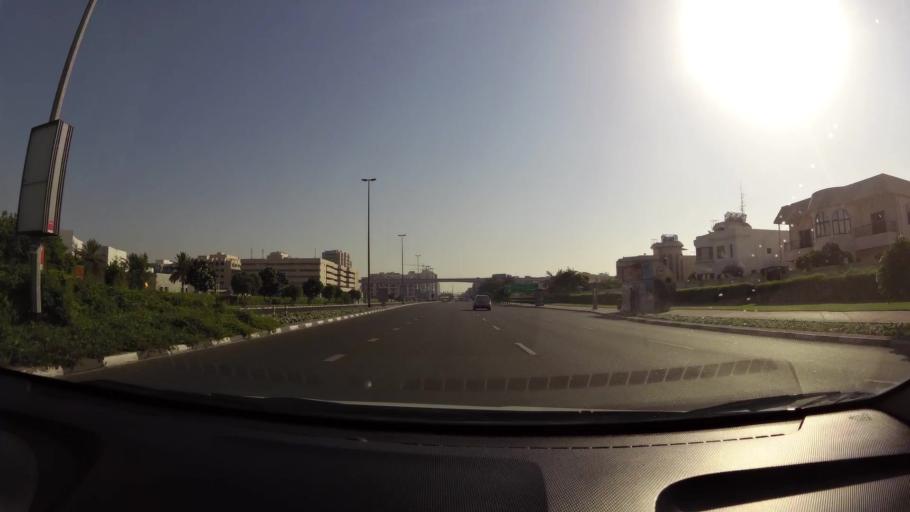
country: AE
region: Ash Shariqah
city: Sharjah
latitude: 25.2653
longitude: 55.3762
